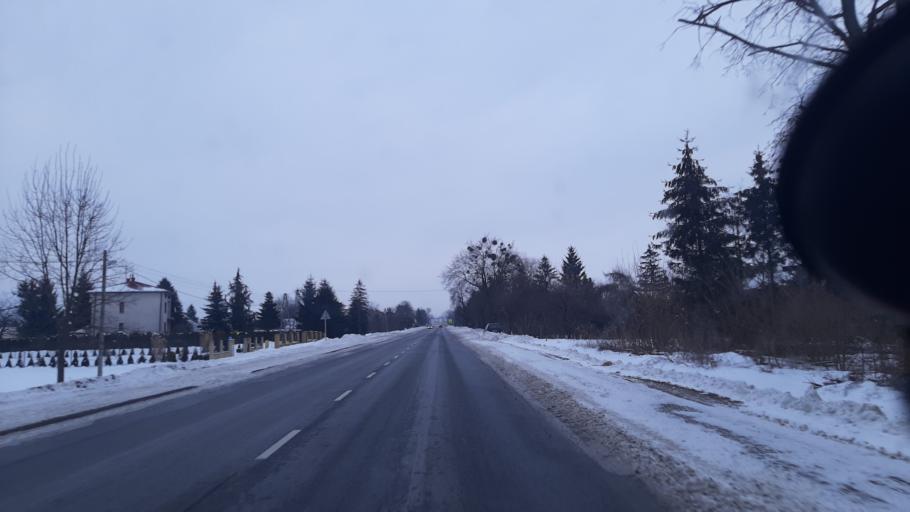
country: PL
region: Lublin Voivodeship
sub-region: Powiat pulawski
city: Markuszow
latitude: 51.3768
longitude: 22.2488
